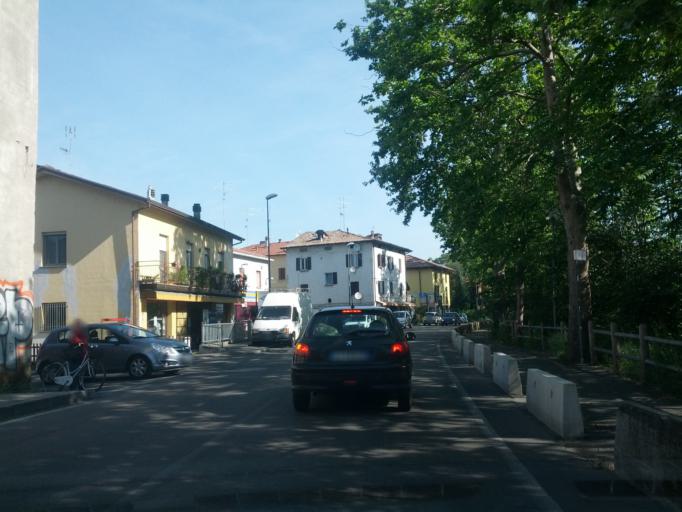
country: IT
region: Emilia-Romagna
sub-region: Provincia di Reggio Emilia
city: Reggio nell'Emilia
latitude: 44.7008
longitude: 10.6176
